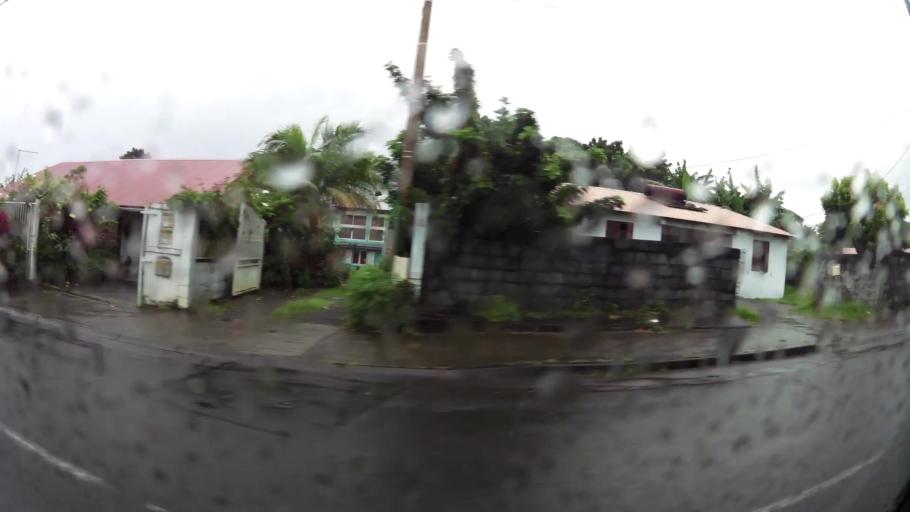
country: RE
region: Reunion
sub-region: Reunion
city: Saint-Benoit
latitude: -21.0227
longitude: 55.6982
